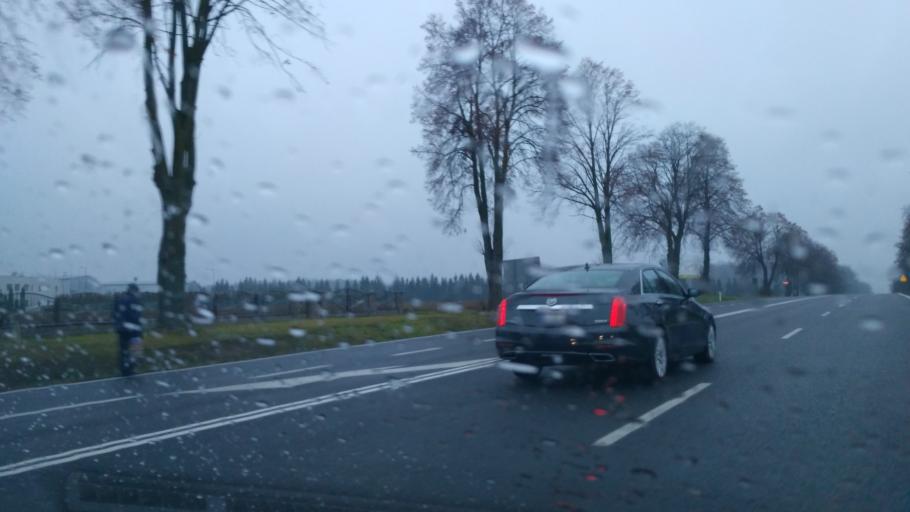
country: PL
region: Subcarpathian Voivodeship
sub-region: Powiat przeworski
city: Debow
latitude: 50.0639
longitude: 22.4356
